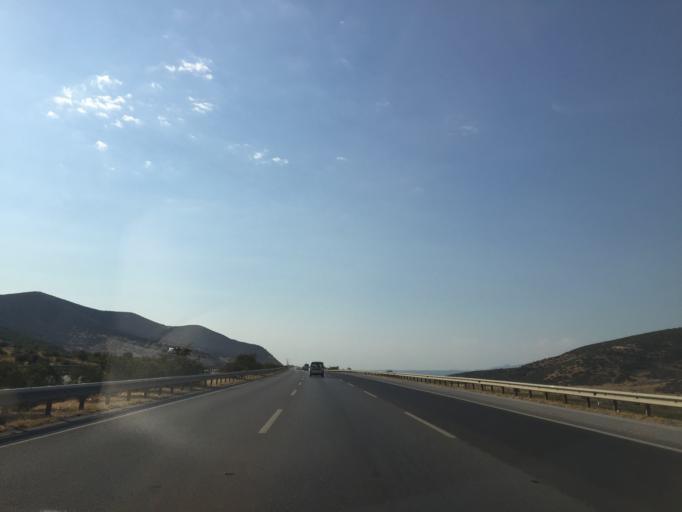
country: TR
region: Izmir
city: Belevi
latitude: 38.0580
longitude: 27.4228
